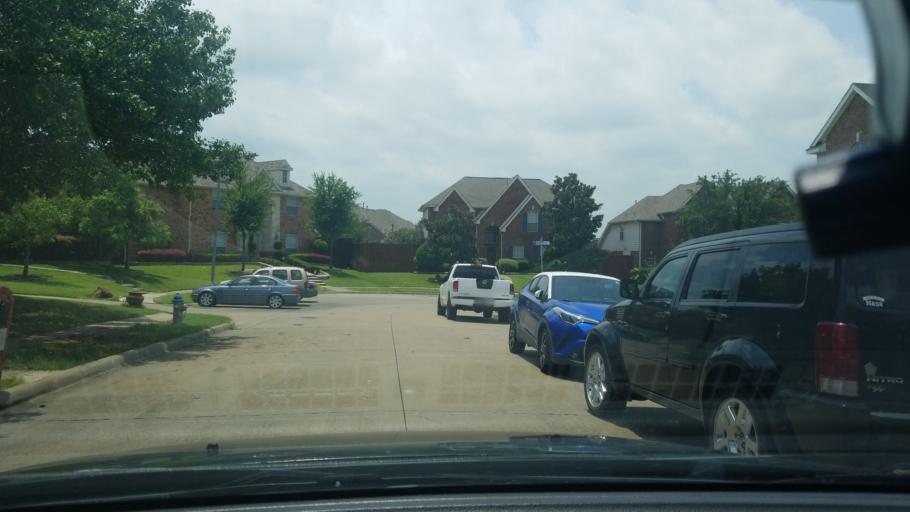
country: US
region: Texas
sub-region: Dallas County
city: Sunnyvale
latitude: 32.8103
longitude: -96.6001
